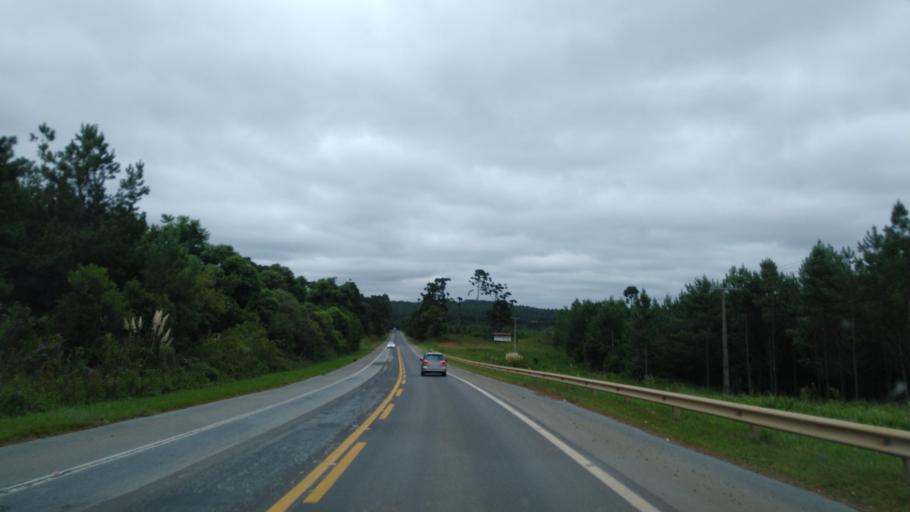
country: BR
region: Santa Catarina
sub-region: Tres Barras
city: Tres Barras
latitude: -26.1616
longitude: -50.1342
